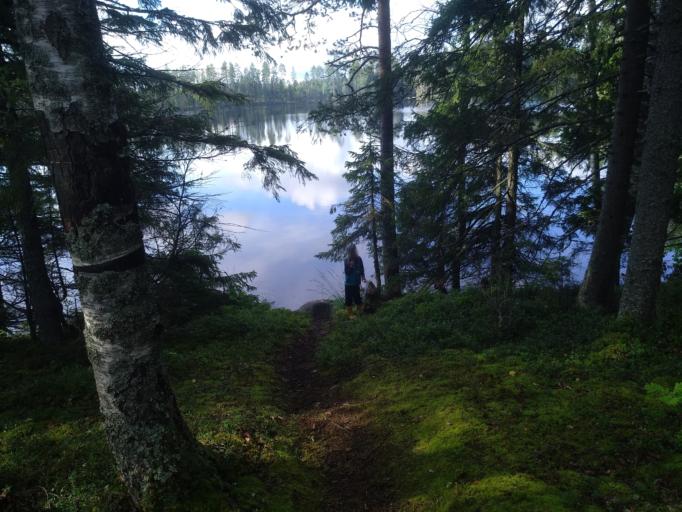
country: RU
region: Republic of Karelia
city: Pryazha
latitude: 61.5353
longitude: 33.4903
